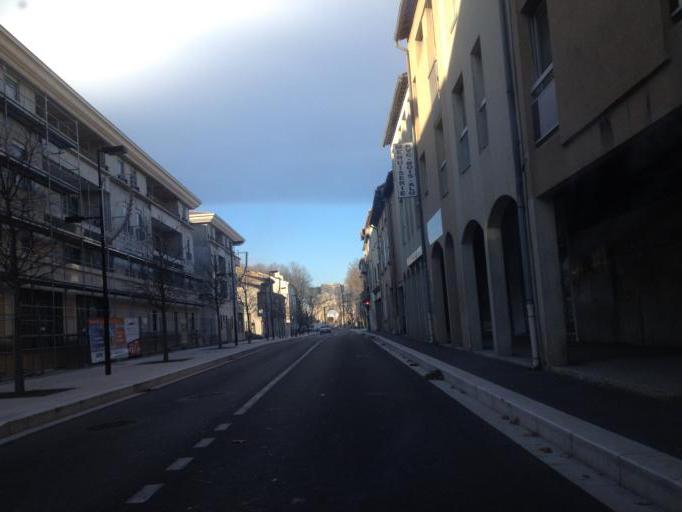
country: FR
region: Provence-Alpes-Cote d'Azur
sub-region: Departement du Vaucluse
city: Orange
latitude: 44.1399
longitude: 4.8057
